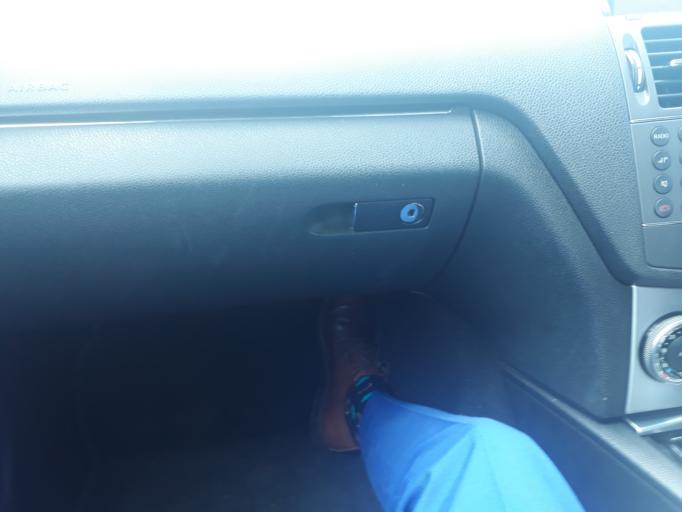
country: BW
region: South East
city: Gaborone
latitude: -24.6735
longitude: 25.8917
